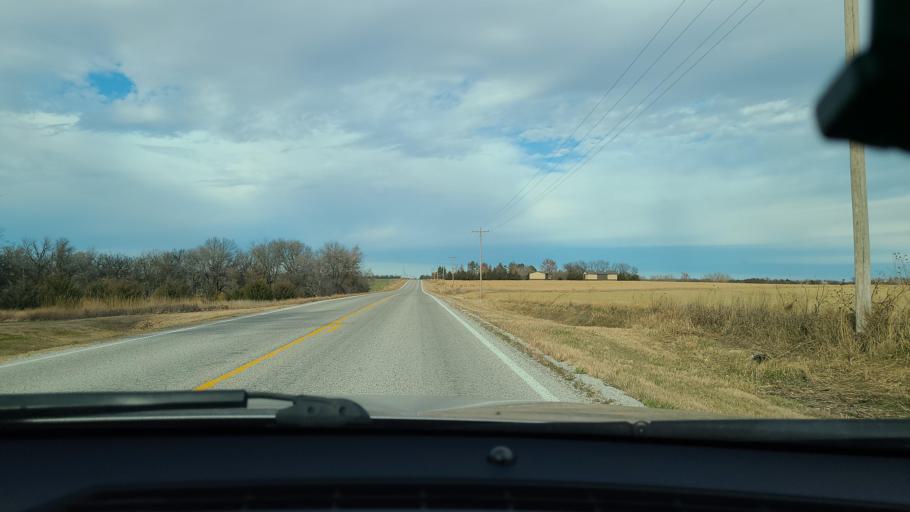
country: US
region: Kansas
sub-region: McPherson County
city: Inman
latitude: 38.2953
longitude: -97.9250
